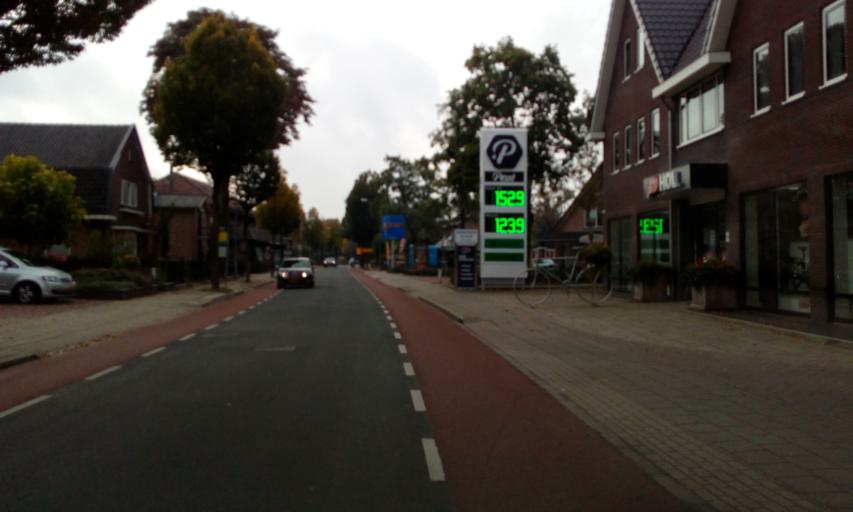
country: NL
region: Gelderland
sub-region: Gemeente Ede
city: Harskamp
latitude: 52.1339
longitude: 5.7502
